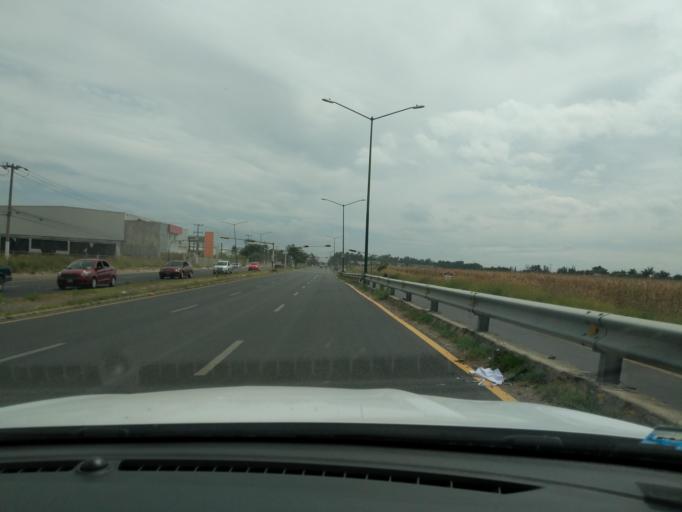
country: MX
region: Jalisco
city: Tesistan
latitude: 20.7906
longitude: -103.4755
